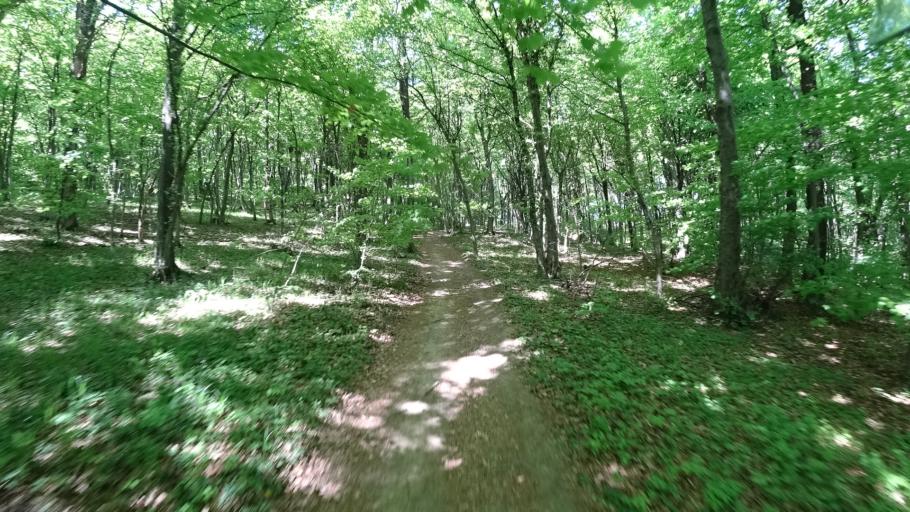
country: HR
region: Zagrebacka
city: Jablanovec
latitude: 45.8609
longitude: 15.8830
